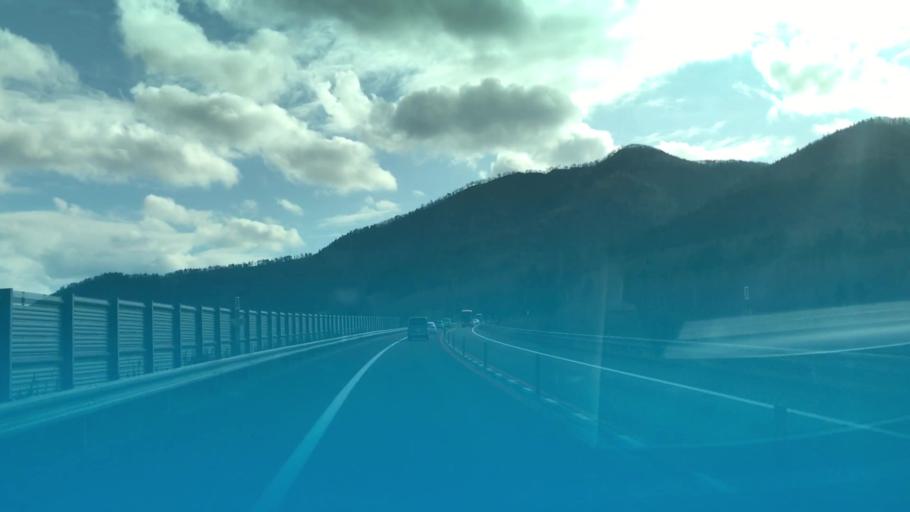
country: JP
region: Hokkaido
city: Shimo-furano
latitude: 43.0595
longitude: 142.5604
